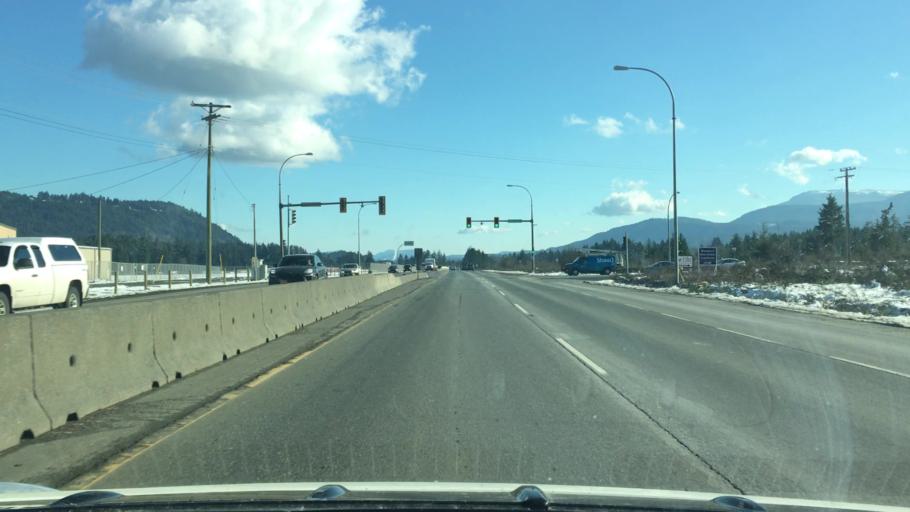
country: CA
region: British Columbia
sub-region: Cowichan Valley Regional District
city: Ladysmith
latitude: 49.0464
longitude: -123.8744
